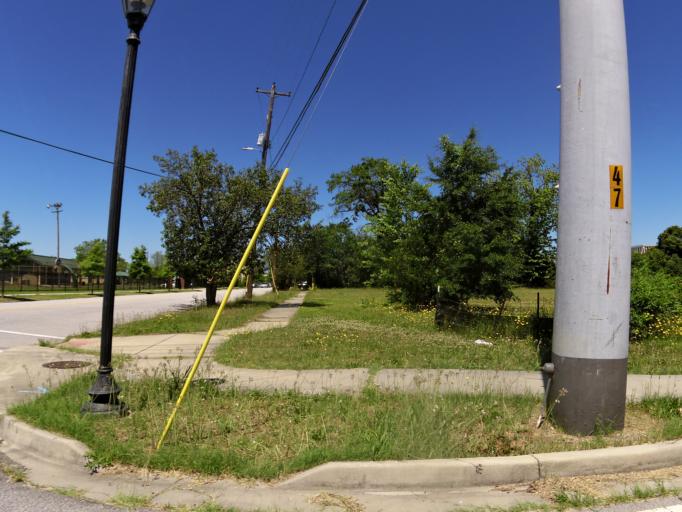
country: US
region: Georgia
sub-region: Richmond County
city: Augusta
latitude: 33.4668
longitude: -81.9697
